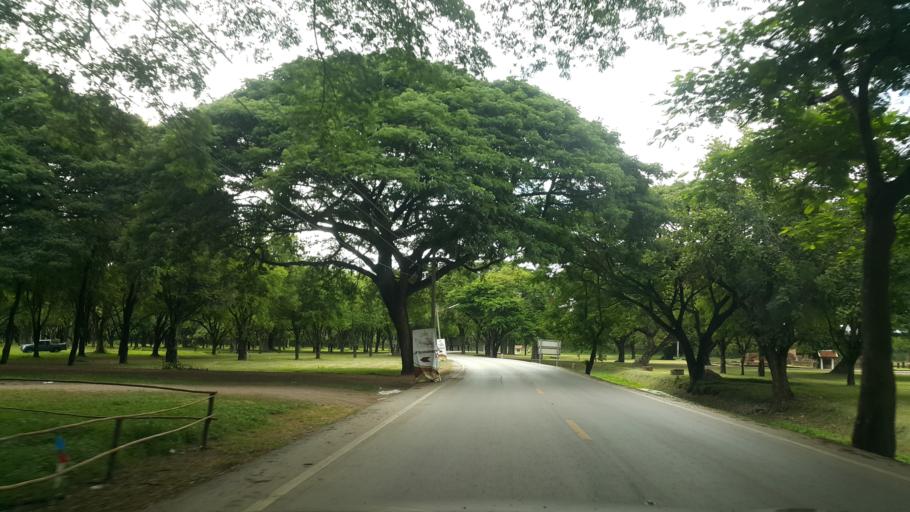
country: TH
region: Sukhothai
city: Ban Na
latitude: 17.0224
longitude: 99.7040
